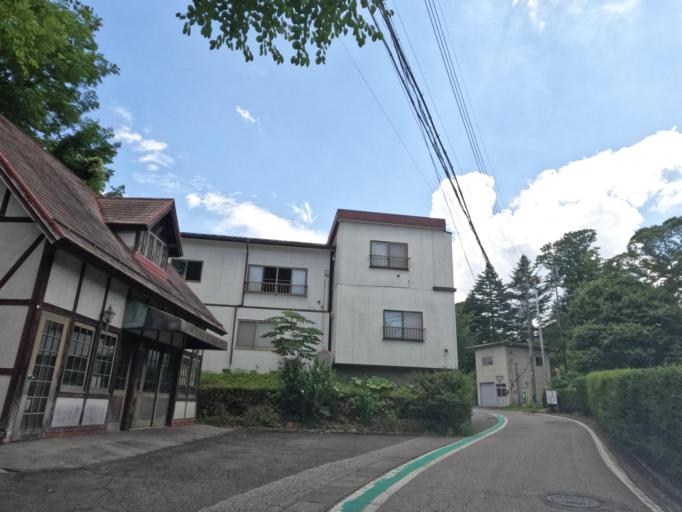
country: JP
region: Nagano
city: Saku
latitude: 36.3316
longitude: 138.6019
